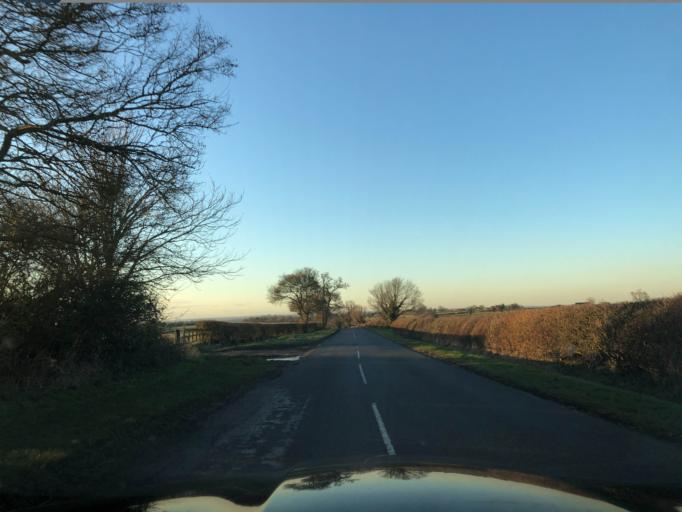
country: GB
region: England
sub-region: Warwickshire
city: Harbury
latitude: 52.2271
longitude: -1.4648
